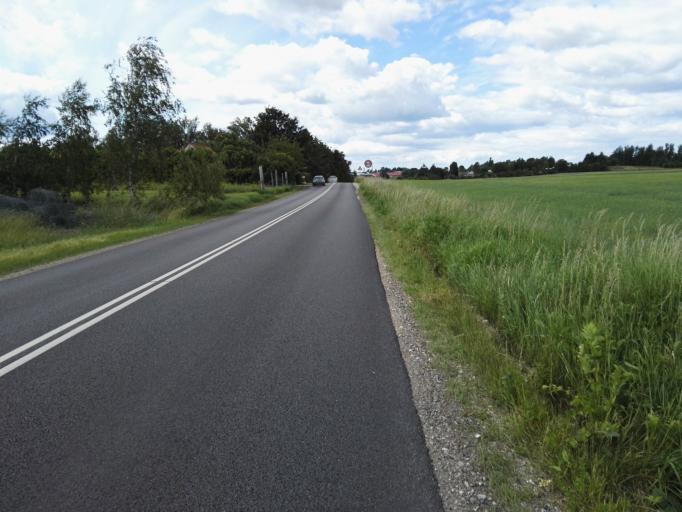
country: DK
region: Capital Region
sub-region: Egedal Kommune
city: Olstykke
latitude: 55.7665
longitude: 12.1547
